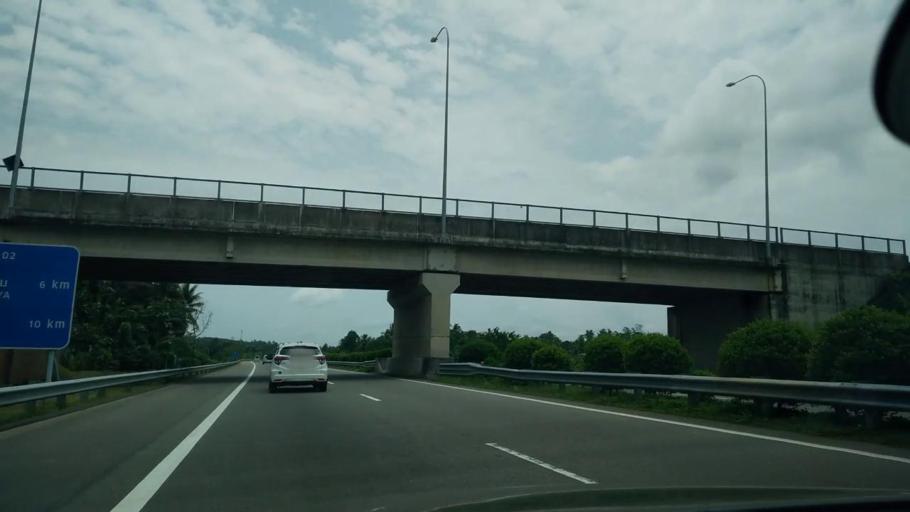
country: LK
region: Western
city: Homagama
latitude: 6.8516
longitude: 79.9784
